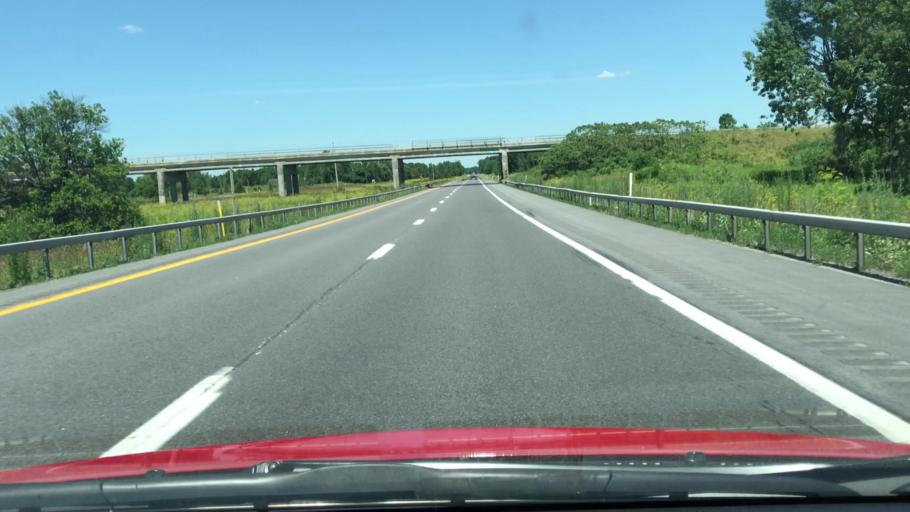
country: US
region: New York
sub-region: Clinton County
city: Cumberland Head
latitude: 44.8175
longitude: -73.4466
